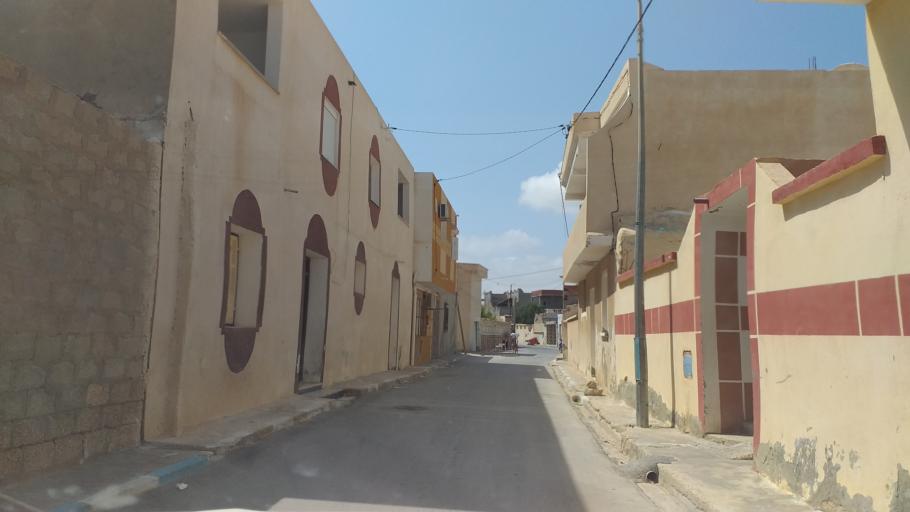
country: TN
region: Qabis
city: Gabes
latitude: 33.9440
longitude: 10.0652
